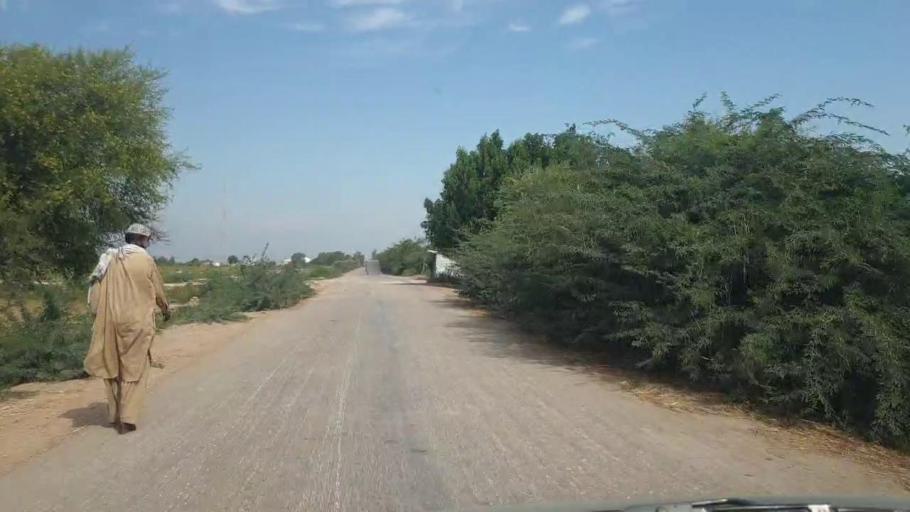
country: PK
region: Sindh
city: Tando Bago
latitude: 24.8882
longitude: 69.0023
